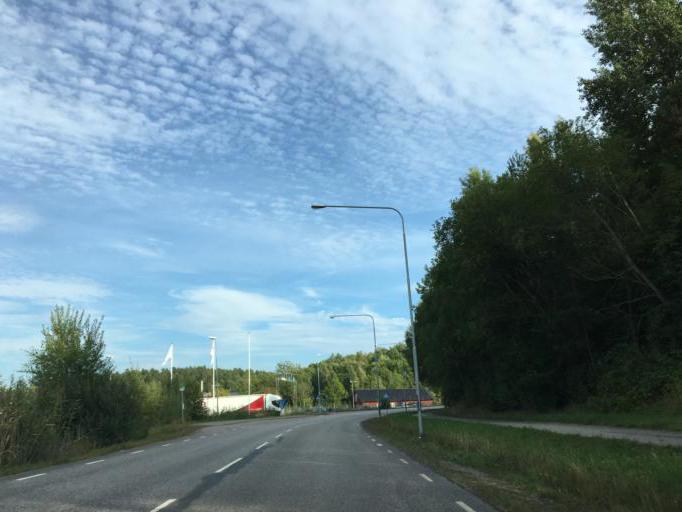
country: SE
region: Soedermanland
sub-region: Eskilstuna Kommun
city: Torshalla
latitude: 59.4279
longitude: 16.4570
